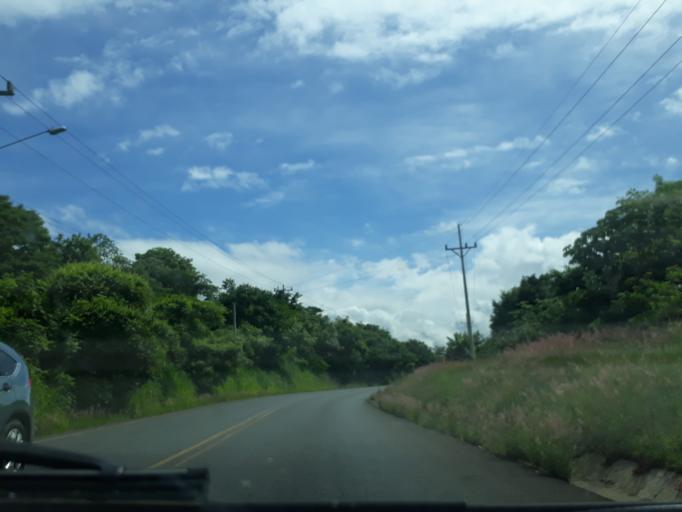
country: CR
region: Alajuela
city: Atenas
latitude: 10.0292
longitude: -84.3562
